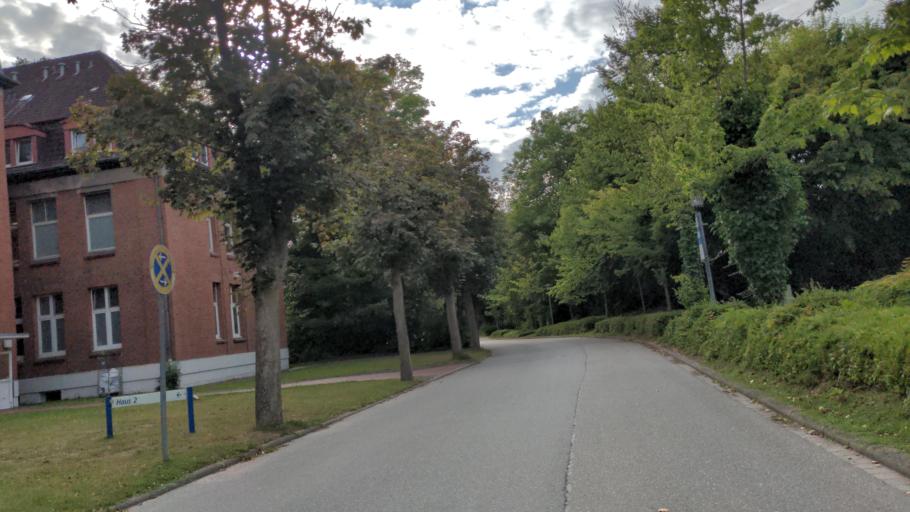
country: DE
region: Schleswig-Holstein
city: Neustadt in Holstein
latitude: 54.1042
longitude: 10.7960
